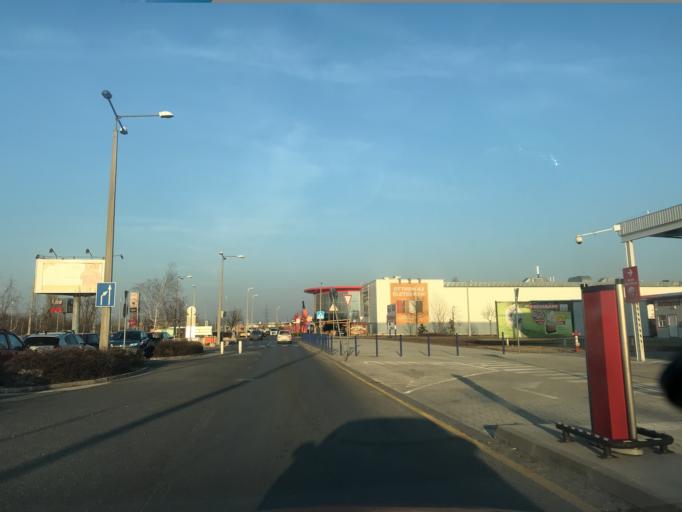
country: HU
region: Gyor-Moson-Sopron
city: Gyor
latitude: 47.6494
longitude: 17.6268
